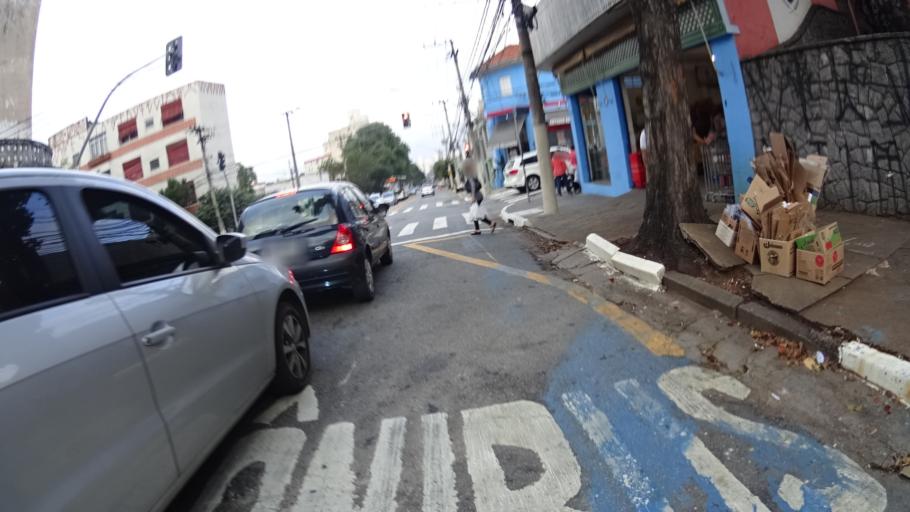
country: BR
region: Sao Paulo
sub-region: Sao Paulo
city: Sao Paulo
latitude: -23.5972
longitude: -46.6305
